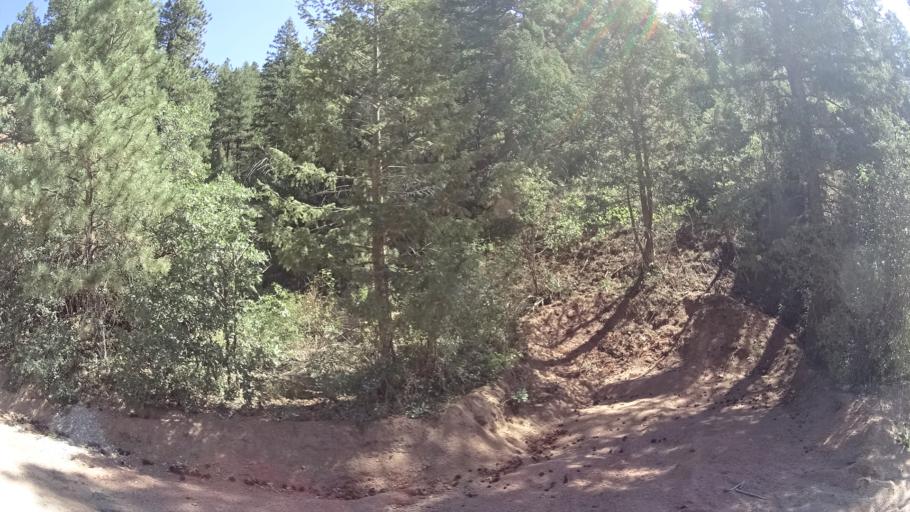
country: US
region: Colorado
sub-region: El Paso County
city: Manitou Springs
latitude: 38.7982
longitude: -104.8827
